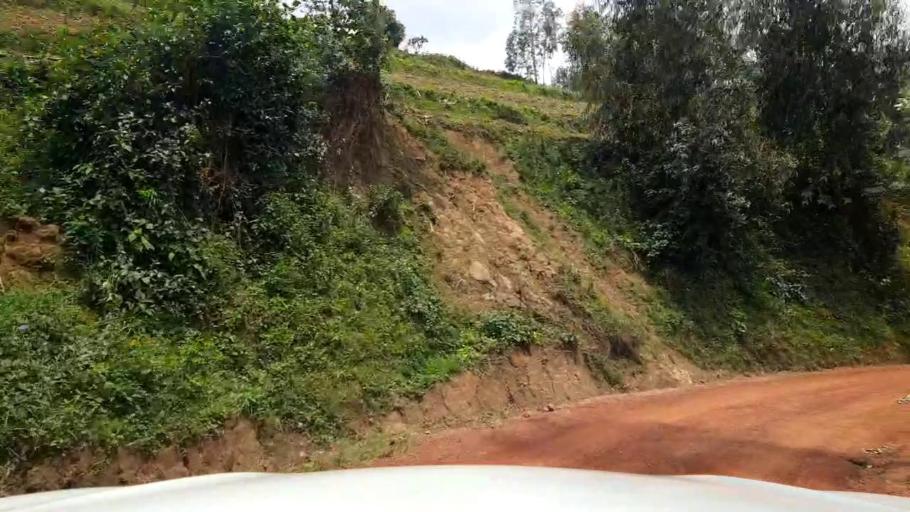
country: RW
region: Northern Province
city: Byumba
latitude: -1.5093
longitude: 29.9378
